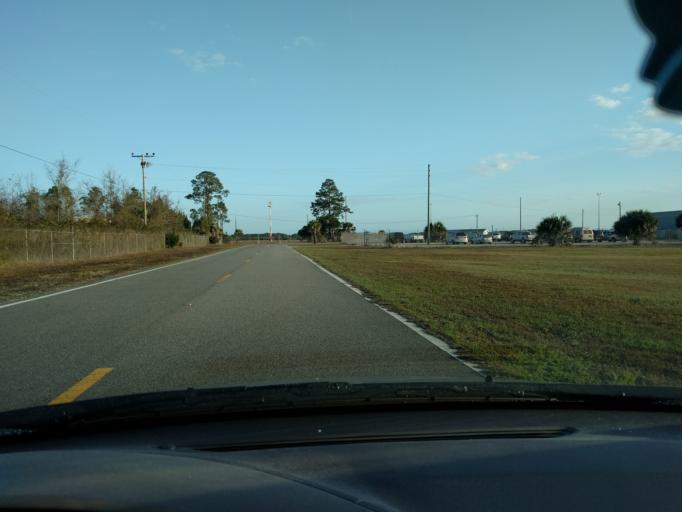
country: US
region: Florida
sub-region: Franklin County
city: Apalachicola
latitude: 29.7218
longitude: -85.0287
